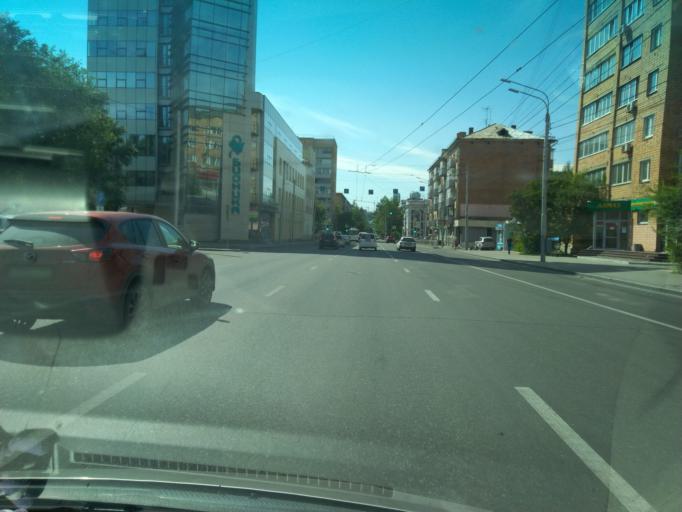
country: RU
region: Krasnoyarskiy
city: Krasnoyarsk
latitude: 56.0120
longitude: 92.8434
